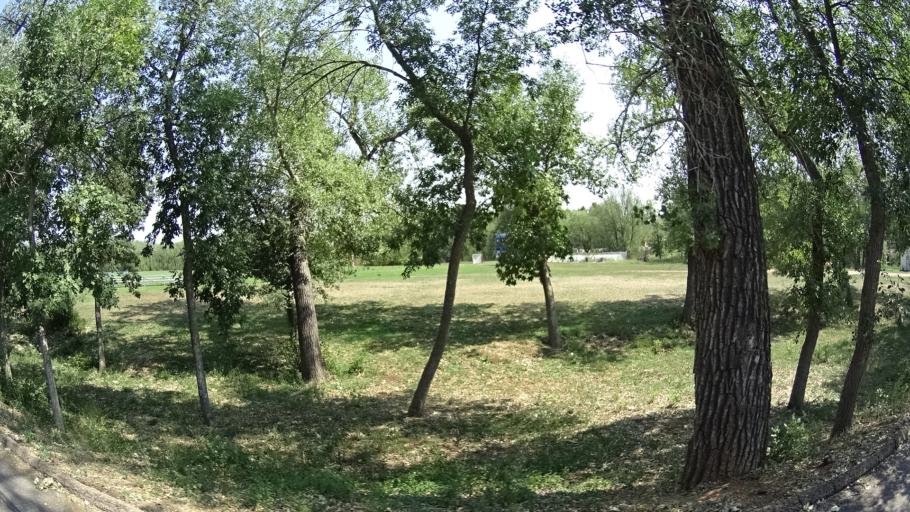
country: US
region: Colorado
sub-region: El Paso County
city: Colorado Springs
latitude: 38.7902
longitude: -104.8392
